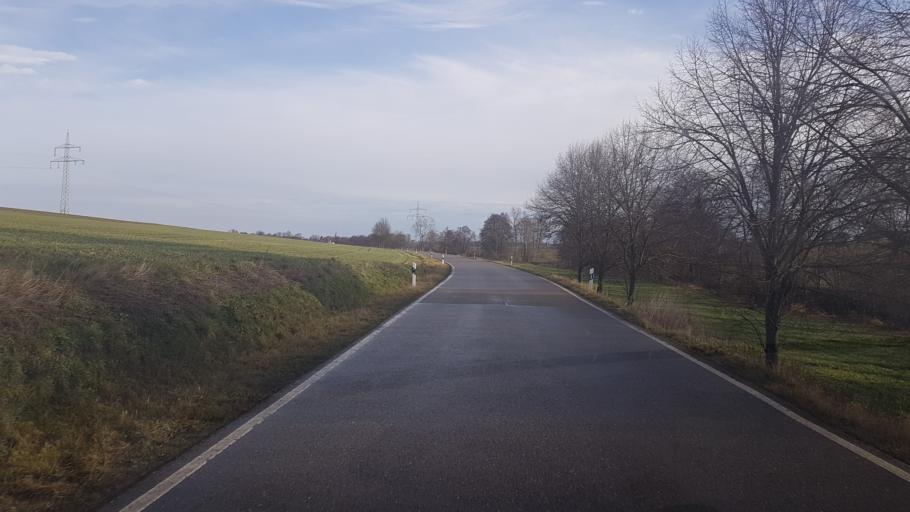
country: DE
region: Baden-Wuerttemberg
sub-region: Regierungsbezirk Stuttgart
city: Wolpertshausen
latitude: 49.2054
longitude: 9.8451
